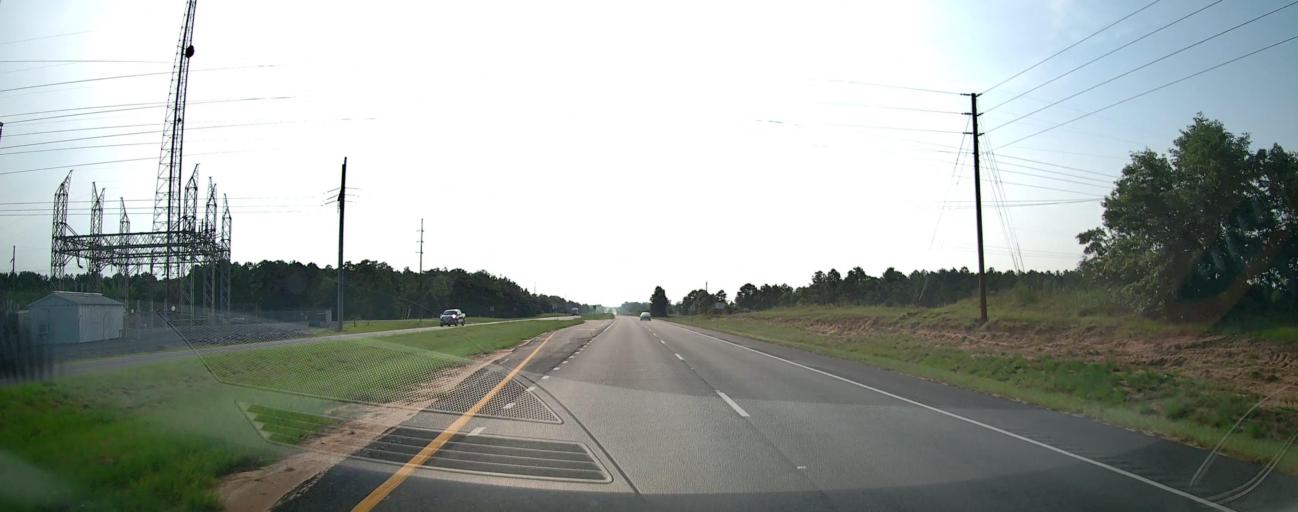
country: US
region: Georgia
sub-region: Taylor County
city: Butler
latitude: 32.5719
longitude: -84.2887
